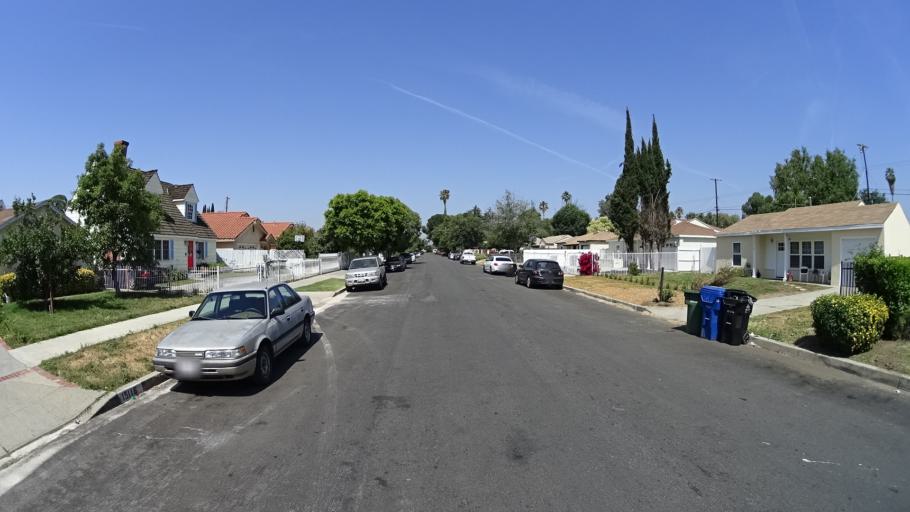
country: US
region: California
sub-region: Los Angeles County
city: Van Nuys
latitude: 34.2039
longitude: -118.4623
